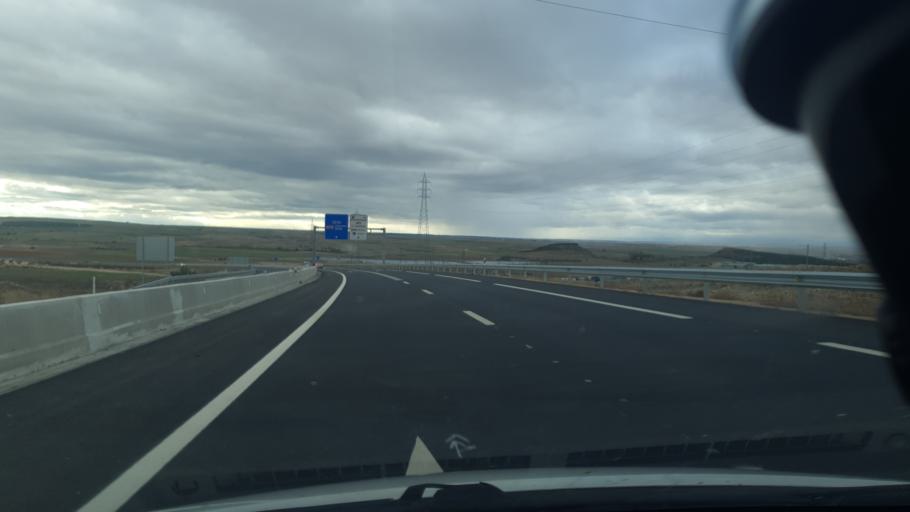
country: ES
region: Castille and Leon
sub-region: Provincia de Segovia
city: Segovia
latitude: 40.9230
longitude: -4.1445
